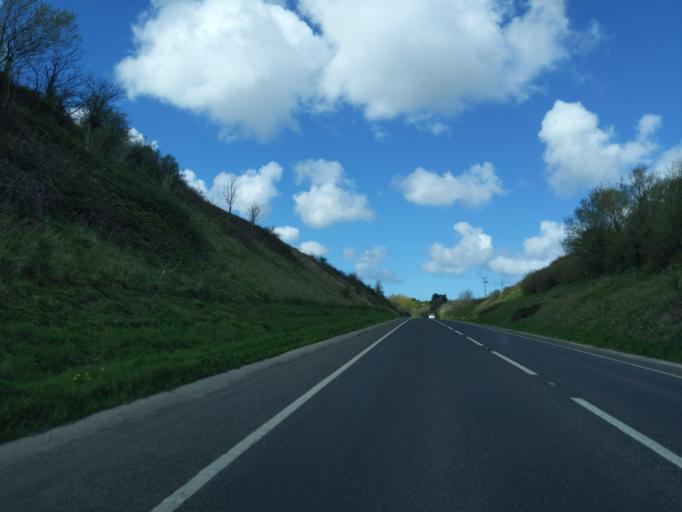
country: GB
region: England
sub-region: Cornwall
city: Wadebridge
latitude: 50.5173
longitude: -4.8194
